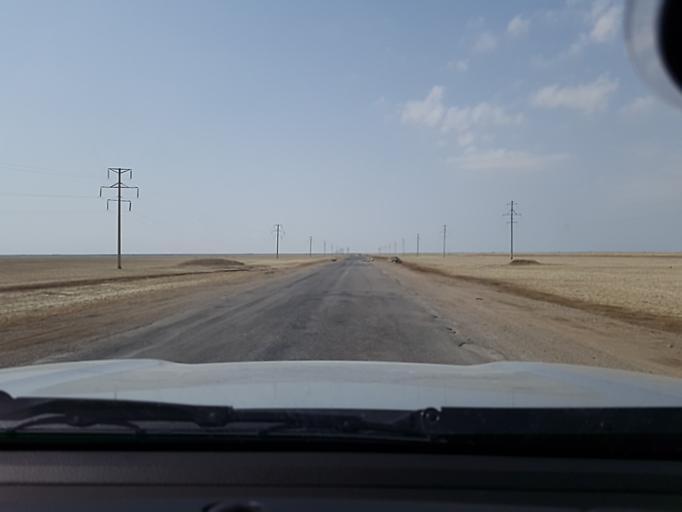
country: TM
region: Balkan
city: Gumdag
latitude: 39.0673
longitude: 54.5843
